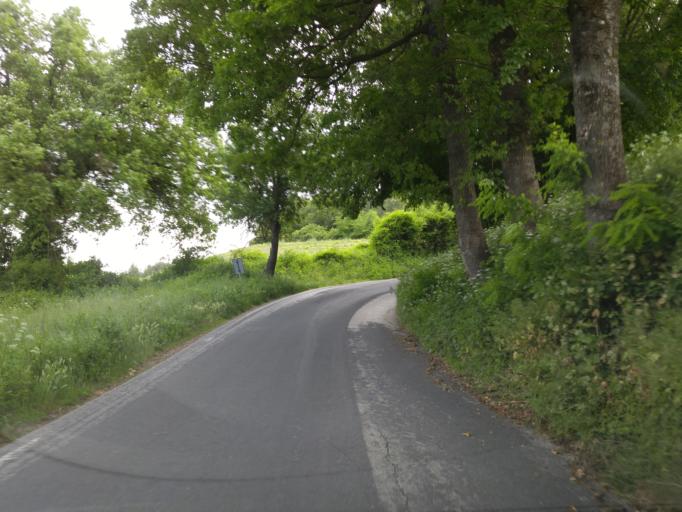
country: IT
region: The Marches
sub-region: Provincia di Pesaro e Urbino
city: Fermignano
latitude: 43.7038
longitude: 12.6374
